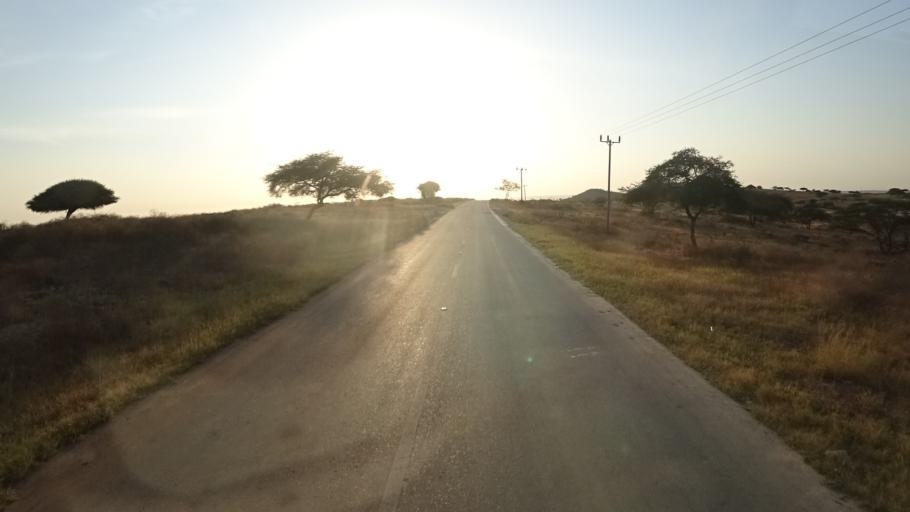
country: OM
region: Zufar
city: Salalah
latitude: 17.1477
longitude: 54.6108
